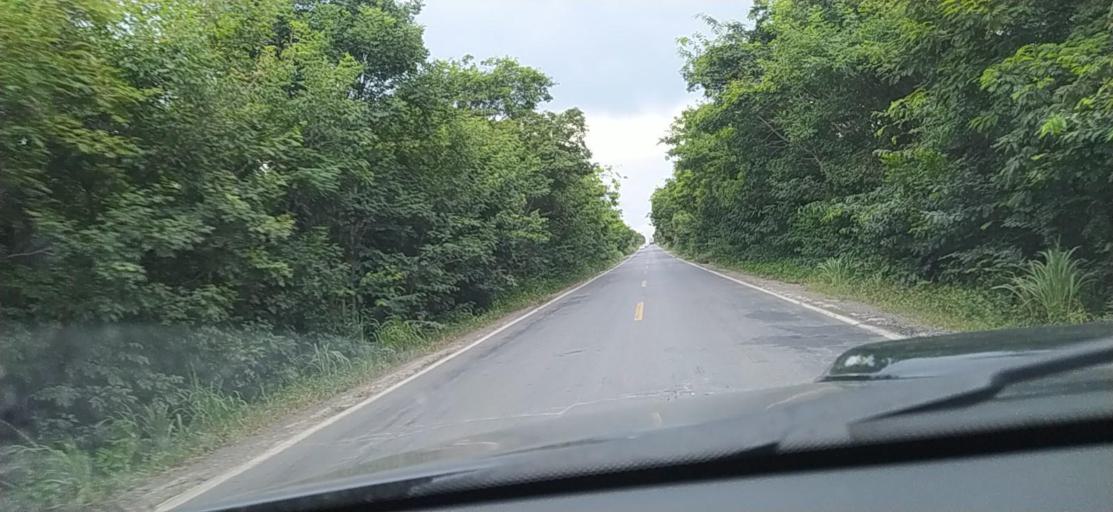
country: BR
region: Minas Gerais
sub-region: Francisco Sa
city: Francisco Sa
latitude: -16.2308
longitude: -43.6138
